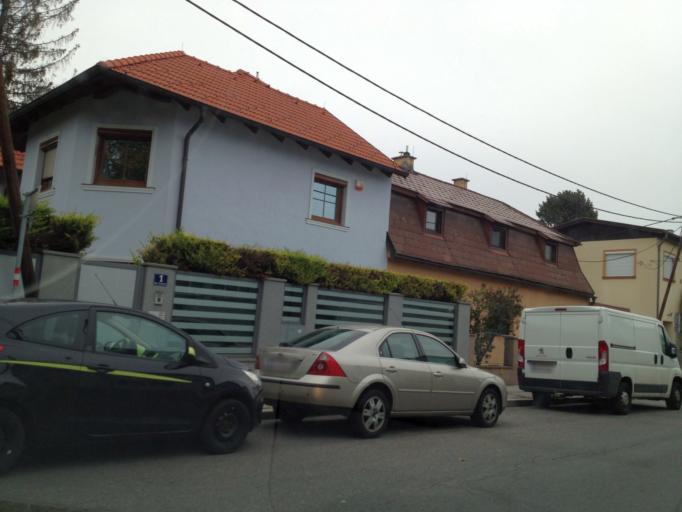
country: AT
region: Lower Austria
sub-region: Politischer Bezirk Korneuburg
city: Langenzersdorf
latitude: 48.2724
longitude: 16.3859
